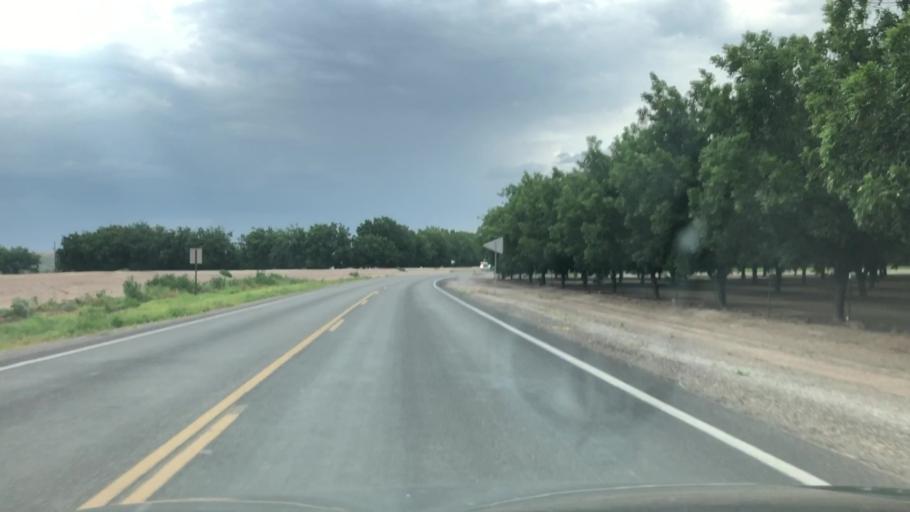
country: US
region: New Mexico
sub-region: Dona Ana County
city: La Union
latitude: 32.0038
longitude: -106.6594
